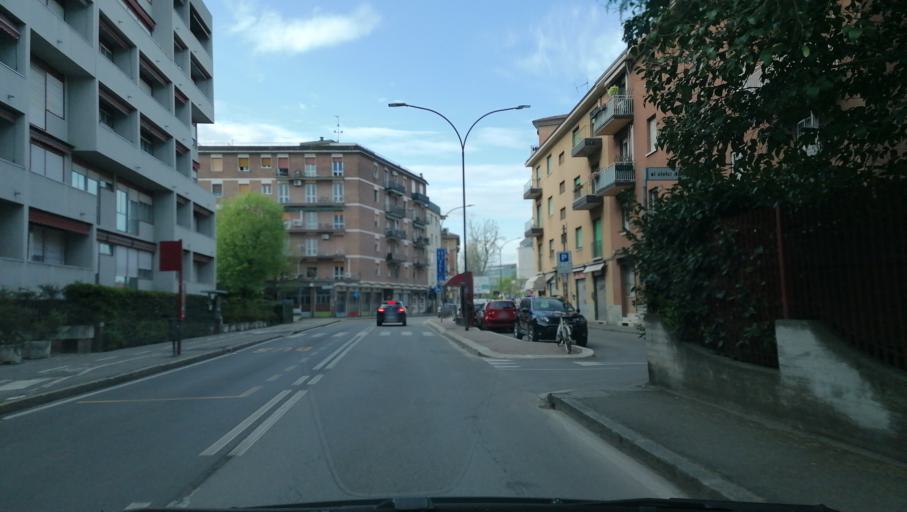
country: IT
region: Emilia-Romagna
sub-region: Provincia di Bologna
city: Bologna
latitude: 44.5142
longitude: 11.3422
